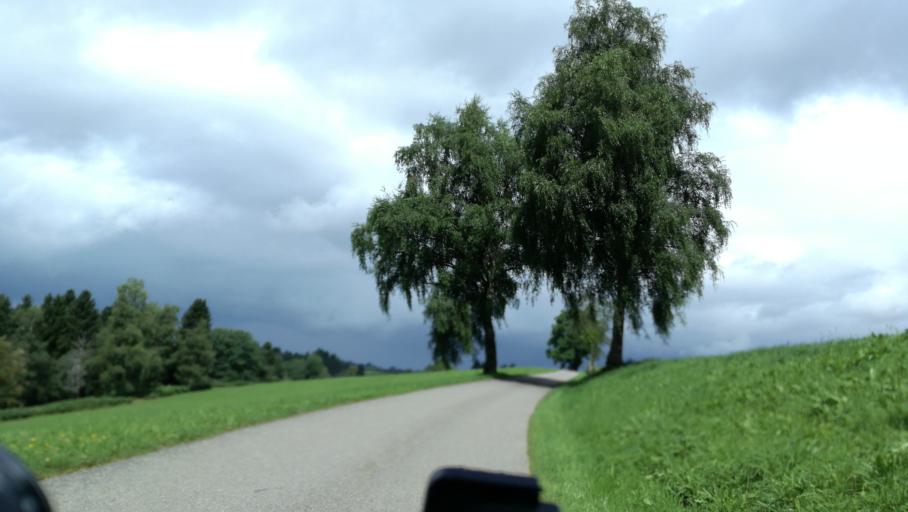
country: CH
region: Zug
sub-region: Zug
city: Walchwil
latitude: 47.1042
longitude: 8.5465
